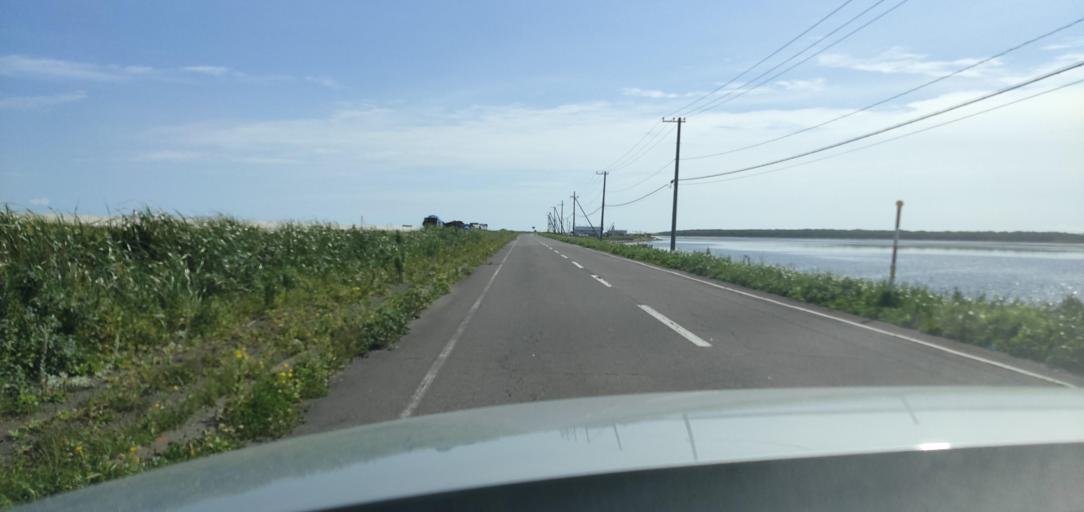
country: JP
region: Hokkaido
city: Shibetsu
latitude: 43.6133
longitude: 145.2504
